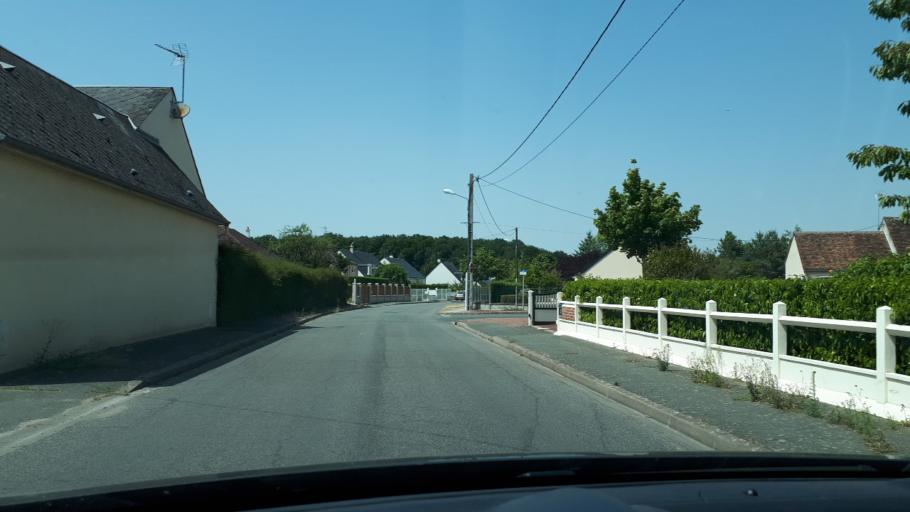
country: FR
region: Centre
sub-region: Departement du Loir-et-Cher
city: Vendome
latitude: 47.8129
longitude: 1.0484
